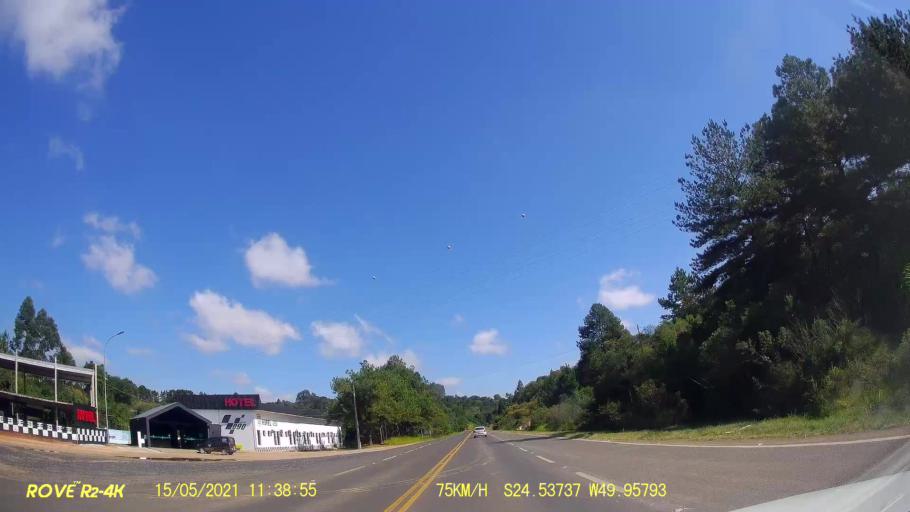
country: BR
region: Parana
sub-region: Pirai Do Sul
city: Pirai do Sul
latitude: -24.5374
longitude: -49.9579
